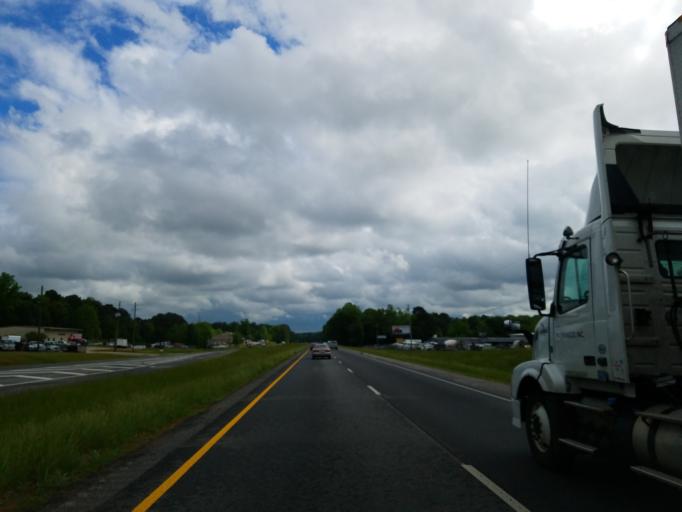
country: US
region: Georgia
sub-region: Spalding County
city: Griffin
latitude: 33.2165
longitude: -84.2889
